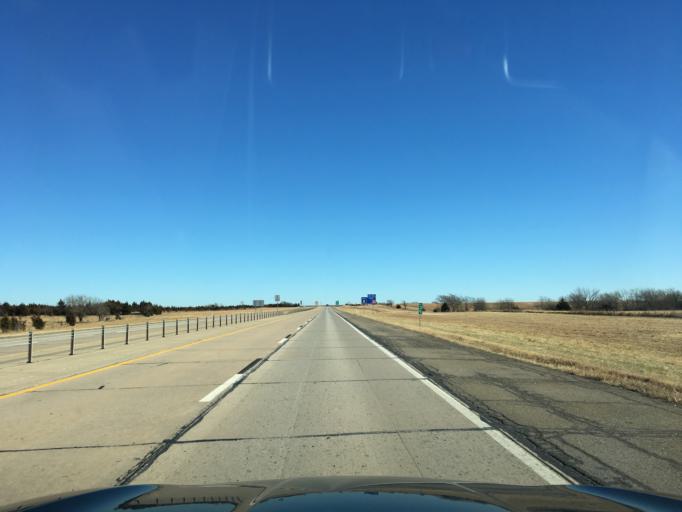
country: US
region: Oklahoma
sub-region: Pawnee County
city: Pawnee
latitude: 36.2247
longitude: -96.8142
